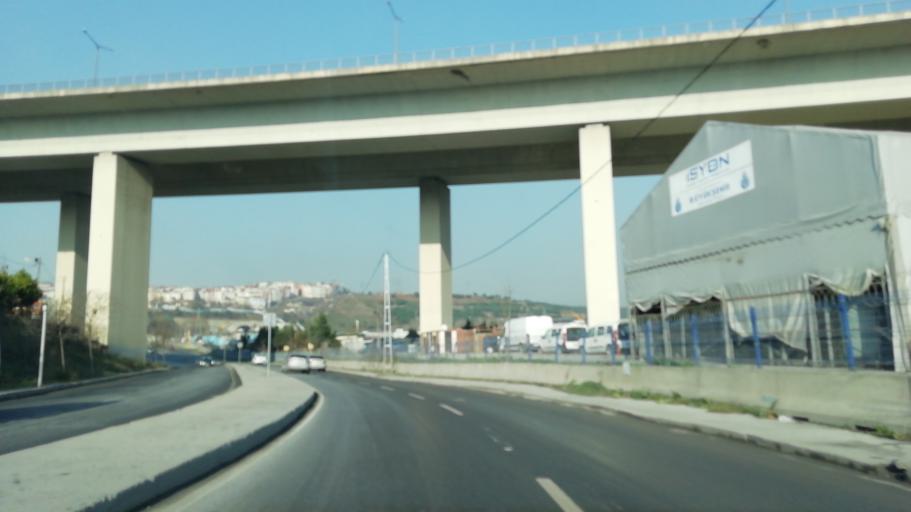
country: TR
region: Istanbul
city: Sultangazi
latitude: 41.0937
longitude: 28.9218
